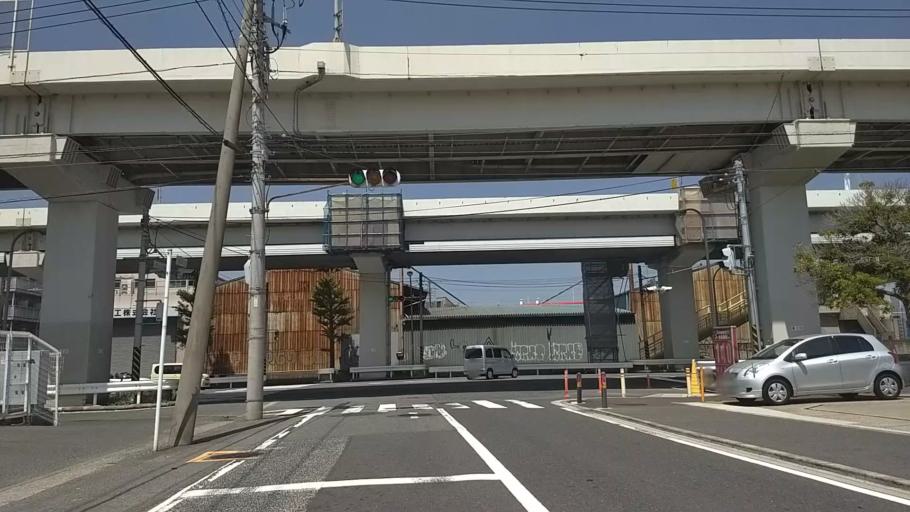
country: JP
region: Kanagawa
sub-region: Kawasaki-shi
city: Kawasaki
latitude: 35.5014
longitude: 139.6981
